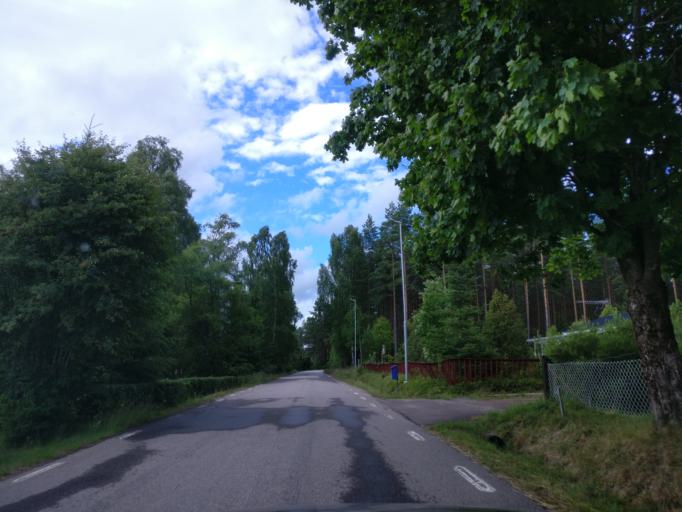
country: SE
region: Vaermland
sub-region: Munkfors Kommun
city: Munkfors
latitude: 59.9748
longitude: 13.4854
